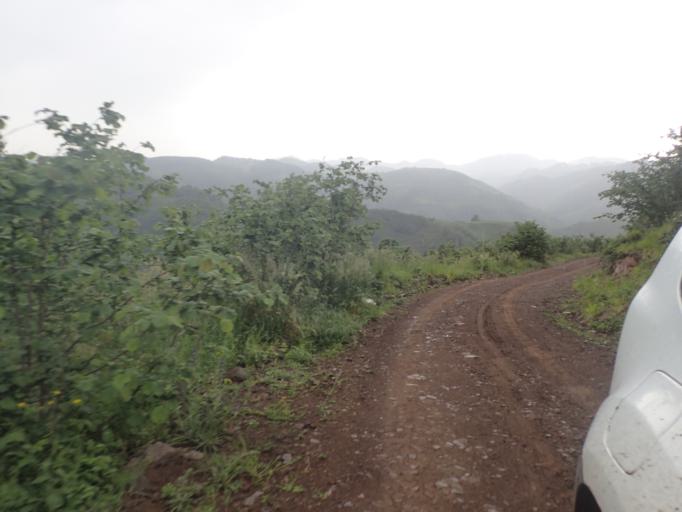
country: TR
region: Samsun
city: Salipazari
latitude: 40.9355
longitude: 36.8664
